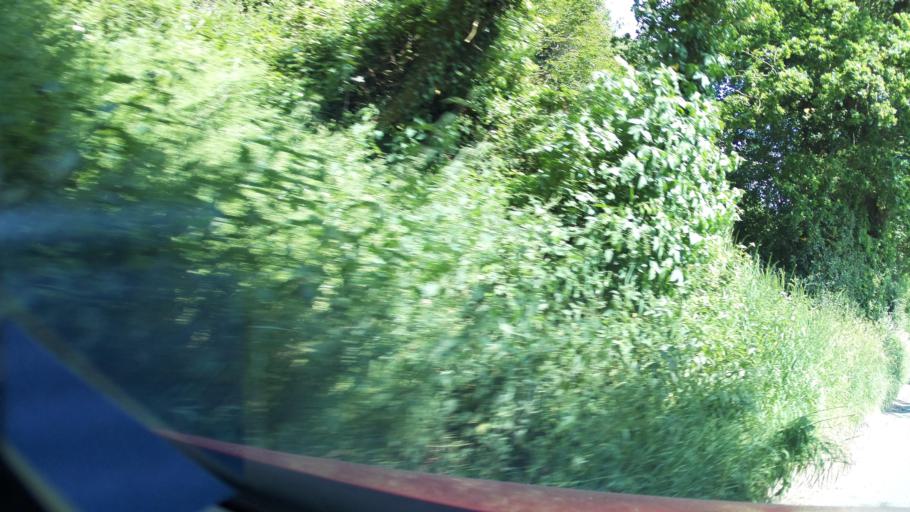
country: GB
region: England
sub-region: Wiltshire
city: Pewsey
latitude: 51.3463
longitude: -1.7866
